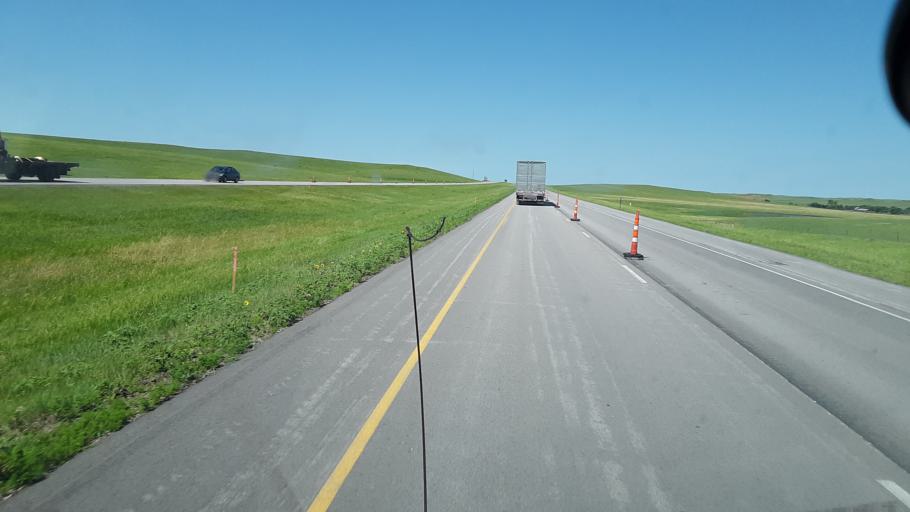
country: US
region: South Dakota
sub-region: Jones County
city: Murdo
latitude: 43.9119
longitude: -100.3489
